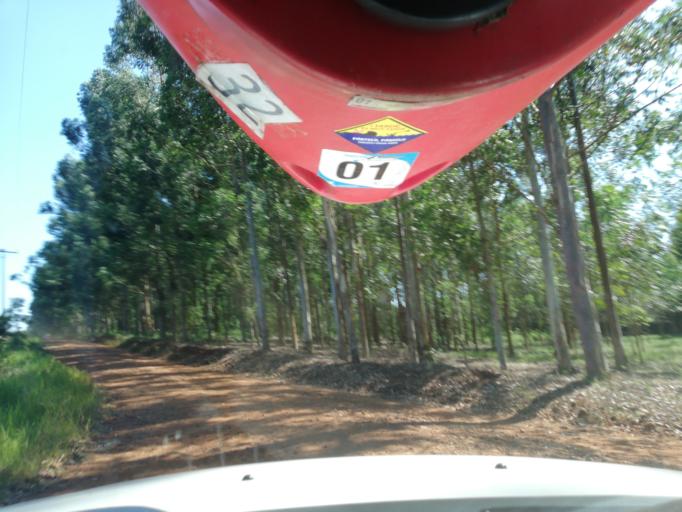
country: AR
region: Misiones
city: Puerto Leoni
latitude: -26.9680
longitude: -55.1527
